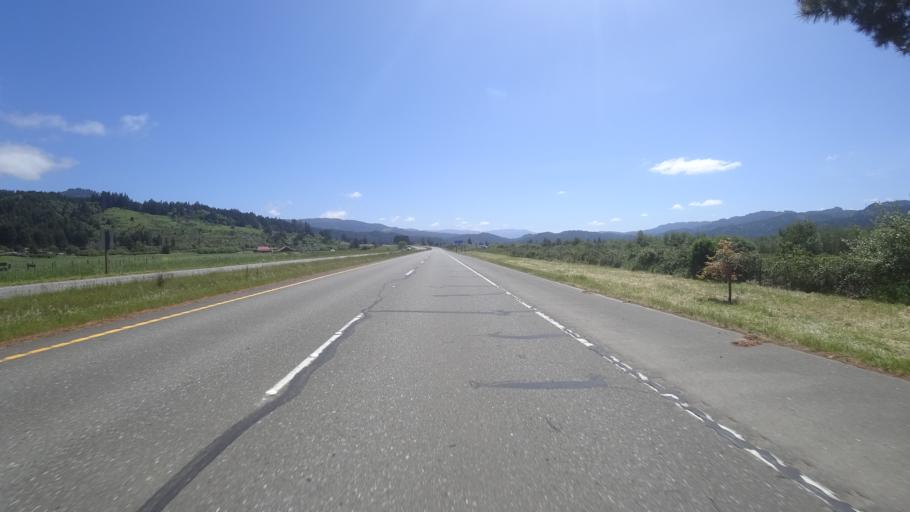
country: US
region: California
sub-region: Humboldt County
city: Blue Lake
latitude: 40.8918
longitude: -124.0090
